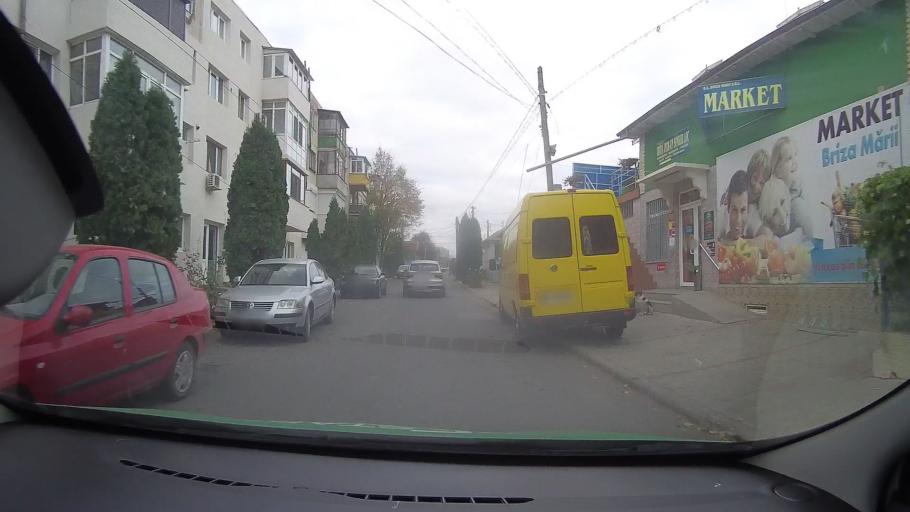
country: RO
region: Tulcea
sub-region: Comuna Jurilovca
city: Jurilovca
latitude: 44.7579
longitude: 28.8758
